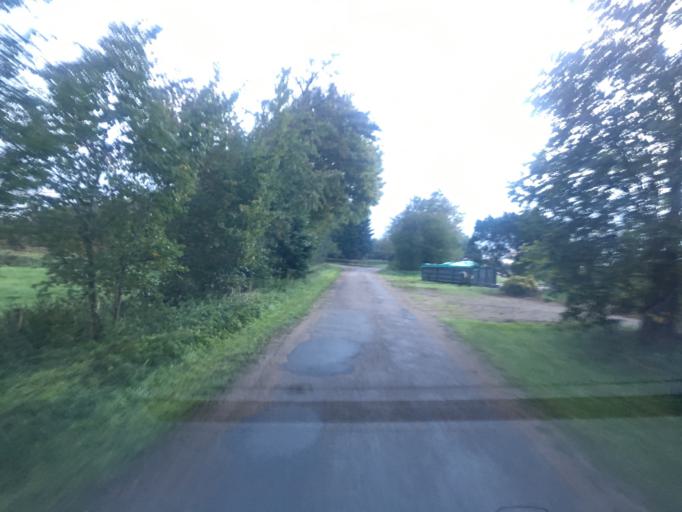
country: DK
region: South Denmark
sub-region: Tonder Kommune
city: Logumkloster
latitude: 54.9857
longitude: 9.0147
